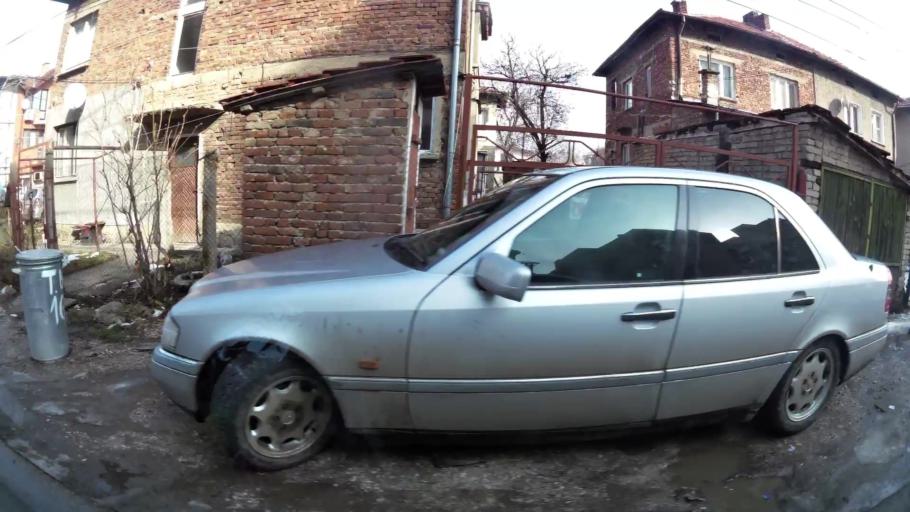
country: BG
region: Sofia-Capital
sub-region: Stolichna Obshtina
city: Sofia
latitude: 42.7223
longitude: 23.2670
